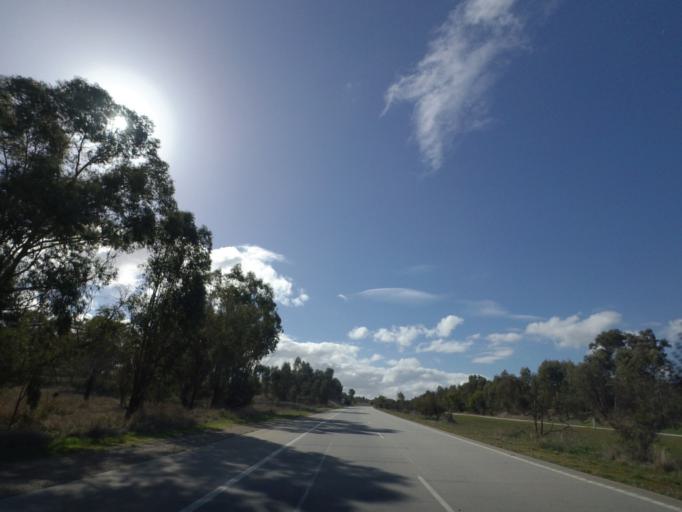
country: AU
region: New South Wales
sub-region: Albury Municipality
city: Lavington
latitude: -36.0323
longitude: 146.9762
